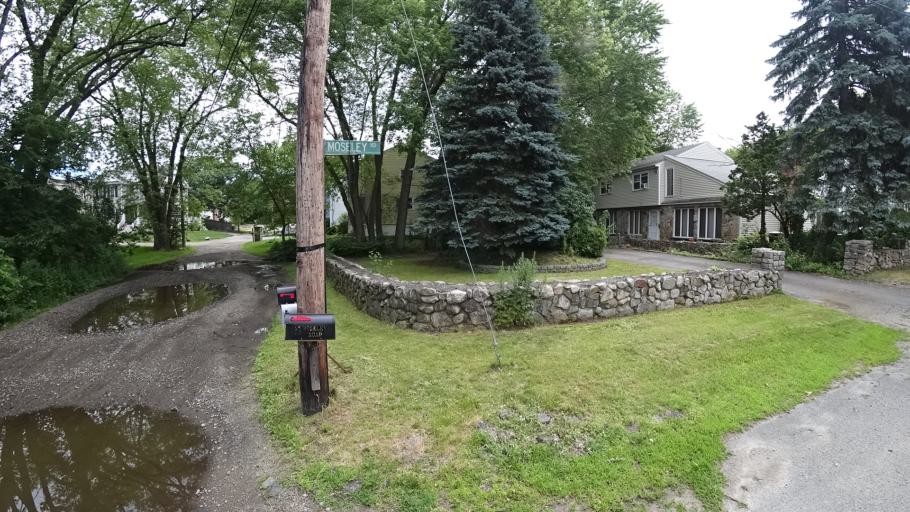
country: US
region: Massachusetts
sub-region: Norfolk County
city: Dedham
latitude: 42.2312
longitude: -71.1406
